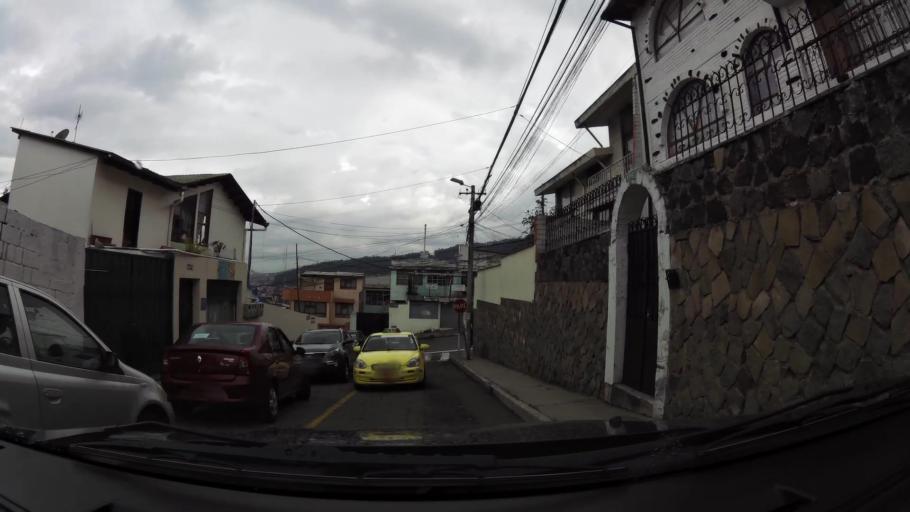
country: EC
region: Pichincha
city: Quito
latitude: -0.1863
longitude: -78.5066
